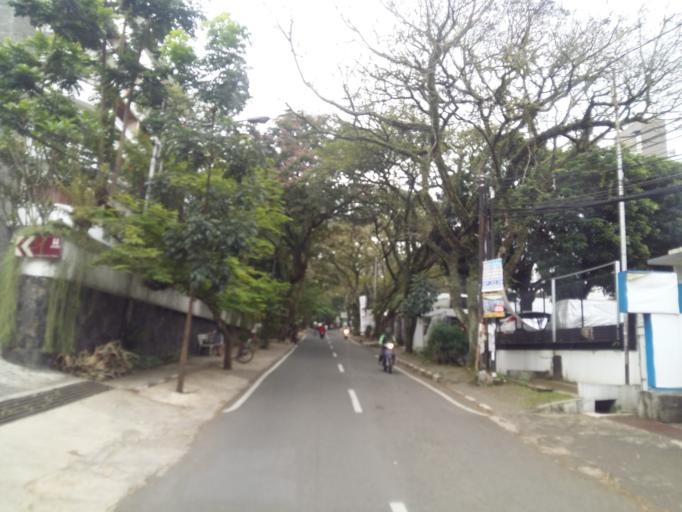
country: ID
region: West Java
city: Bandung
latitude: -6.8845
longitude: 107.6118
